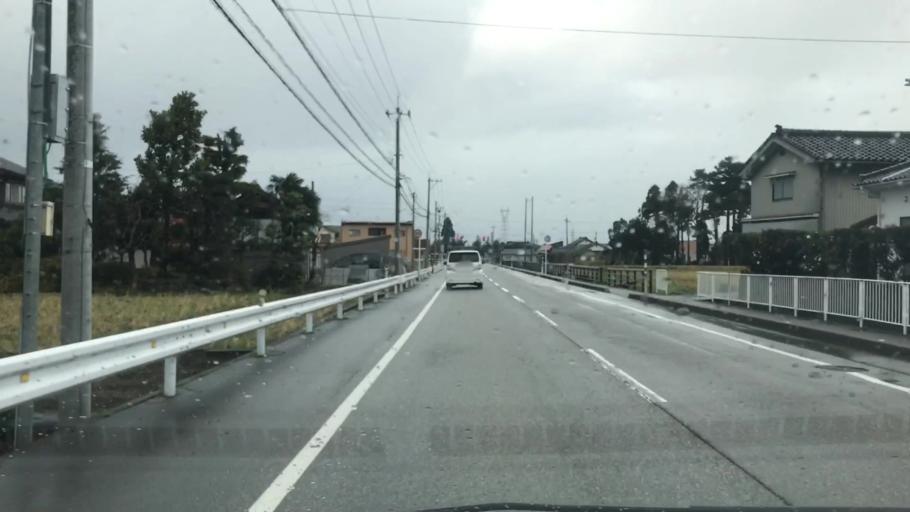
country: JP
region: Toyama
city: Kamiichi
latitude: 36.6768
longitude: 137.2904
